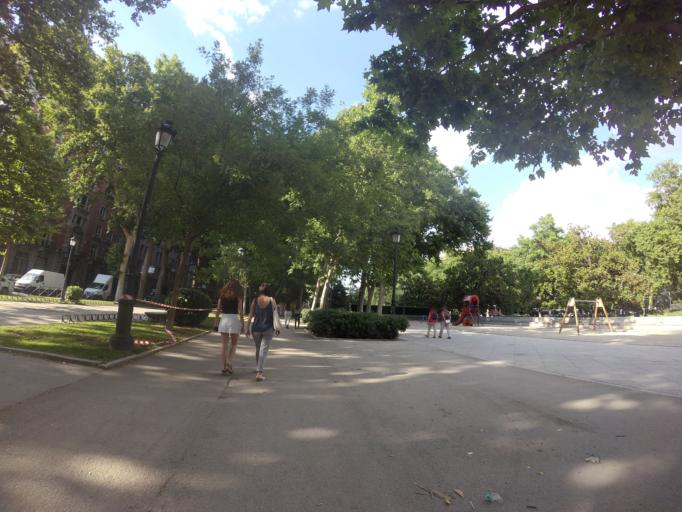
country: ES
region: Madrid
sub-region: Provincia de Madrid
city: Madrid
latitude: 40.4164
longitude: -3.6942
